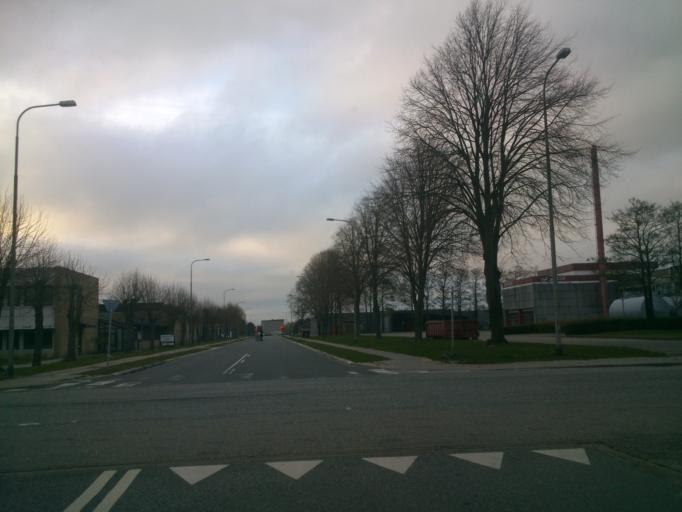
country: DK
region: South Denmark
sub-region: Fredericia Kommune
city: Fredericia
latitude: 55.5672
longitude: 9.7180
